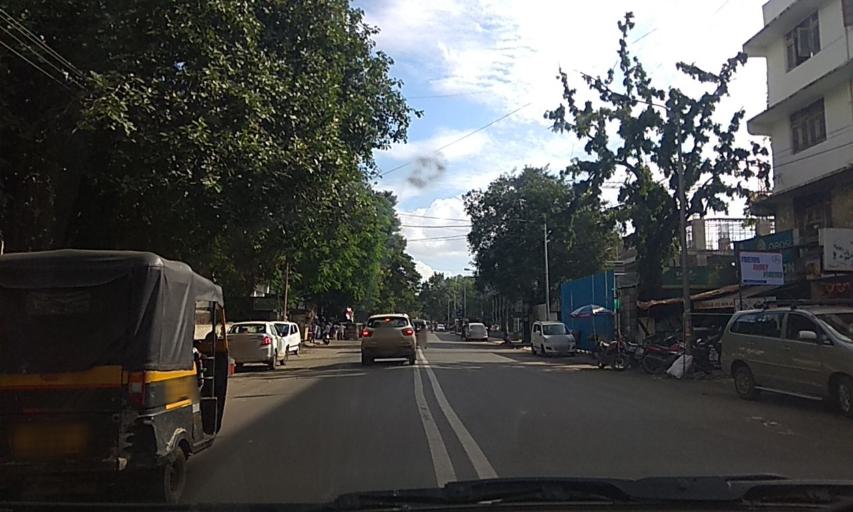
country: IN
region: Maharashtra
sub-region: Pune Division
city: Pune
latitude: 18.5275
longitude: 73.8764
